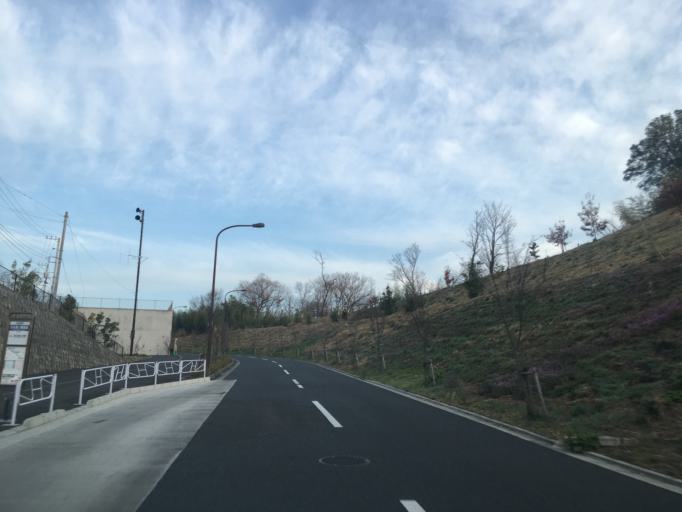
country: JP
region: Tokyo
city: Hino
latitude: 35.6350
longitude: 139.4035
